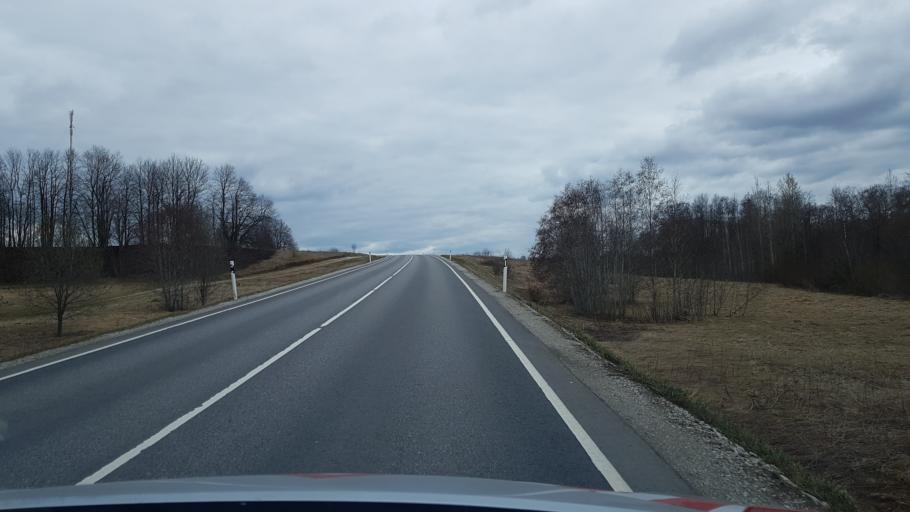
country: EE
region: Ida-Virumaa
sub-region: Narva-Joesuu linn
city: Narva-Joesuu
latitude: 59.4087
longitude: 28.0675
